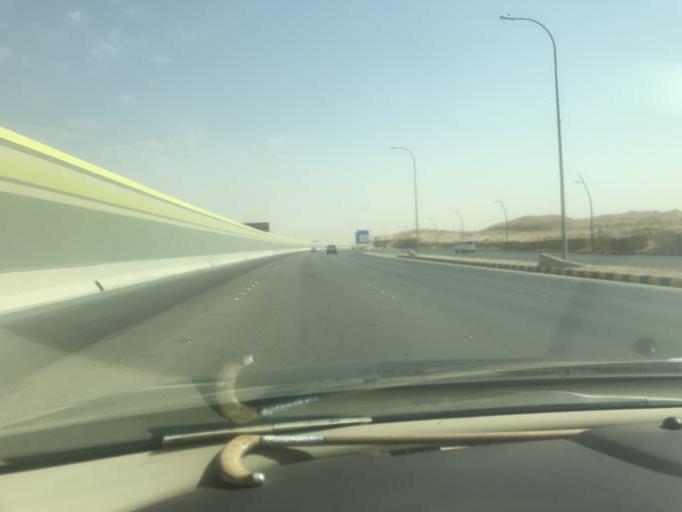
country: SA
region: Ar Riyad
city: Riyadh
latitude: 24.8904
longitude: 46.6951
